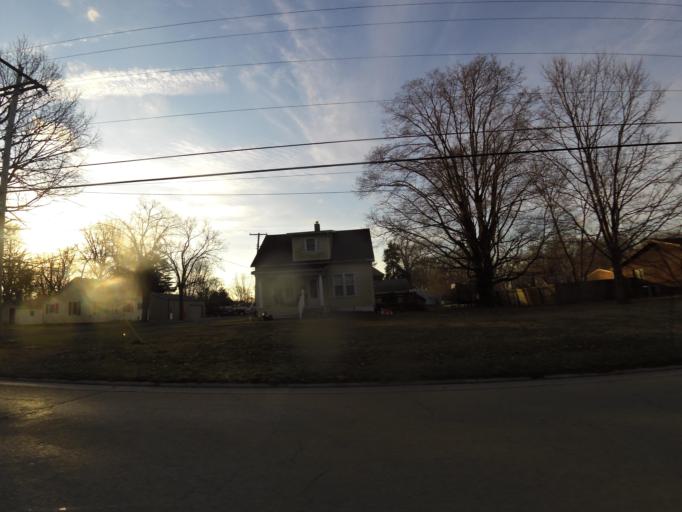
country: US
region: Illinois
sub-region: Fayette County
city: Vandalia
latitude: 38.9575
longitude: -89.1083
